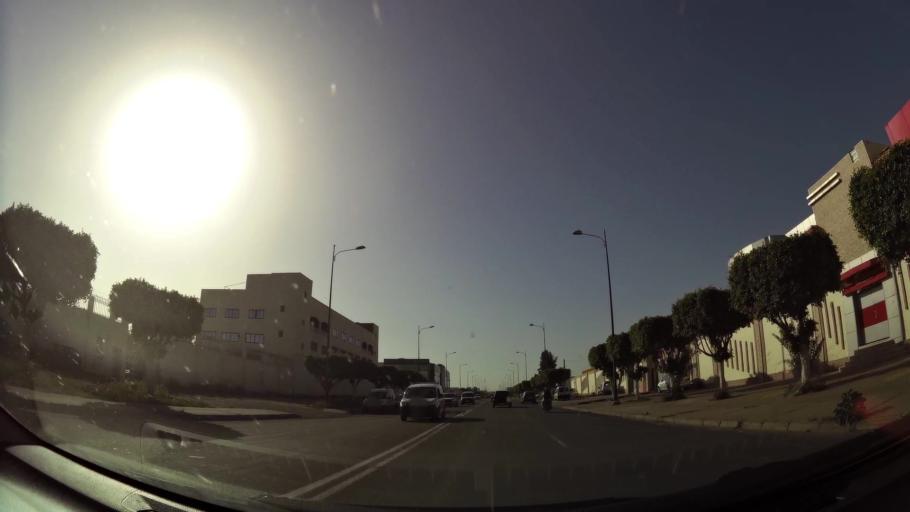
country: MA
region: Souss-Massa-Draa
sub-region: Inezgane-Ait Mellou
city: Inezgane
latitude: 30.3862
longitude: -9.5235
